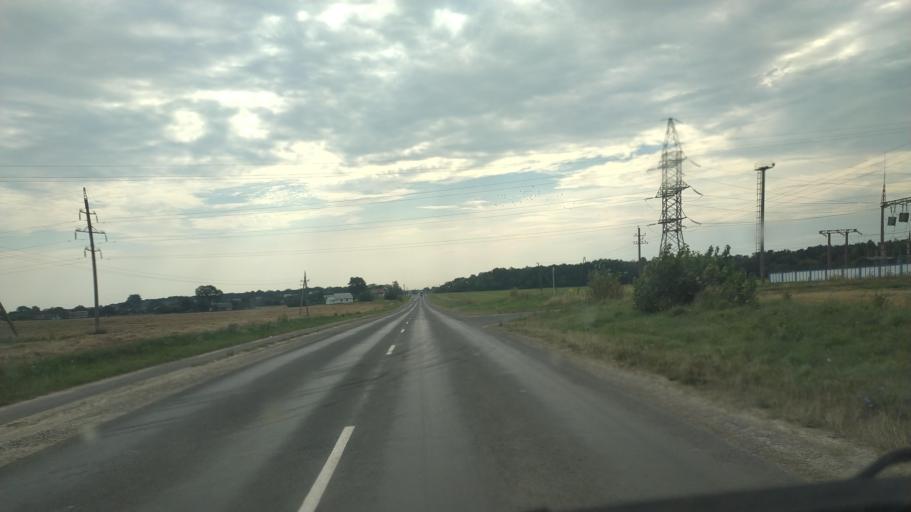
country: BY
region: Brest
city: Byaroza
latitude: 52.5484
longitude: 24.9481
